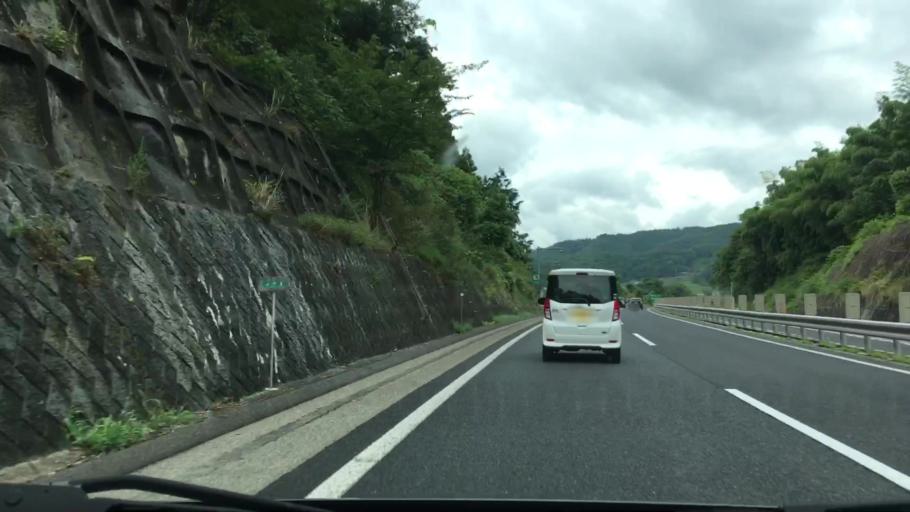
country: JP
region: Okayama
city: Tsuyama
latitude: 35.0153
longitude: 134.2342
